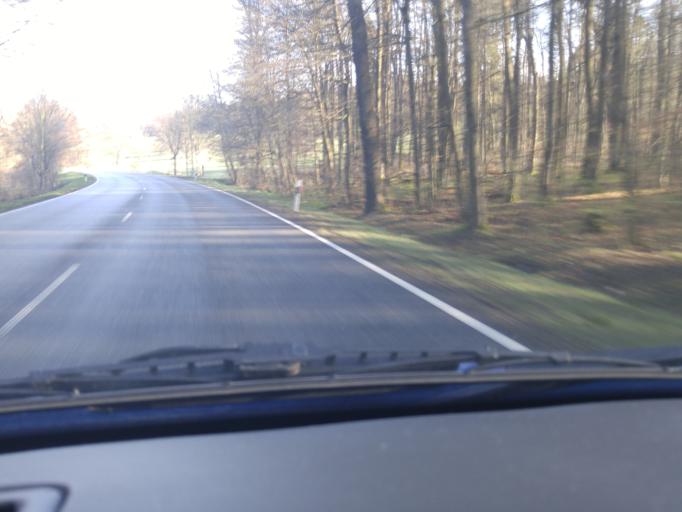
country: DE
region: Hesse
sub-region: Regierungsbezirk Giessen
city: Lauterbach
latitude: 50.6087
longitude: 9.3923
